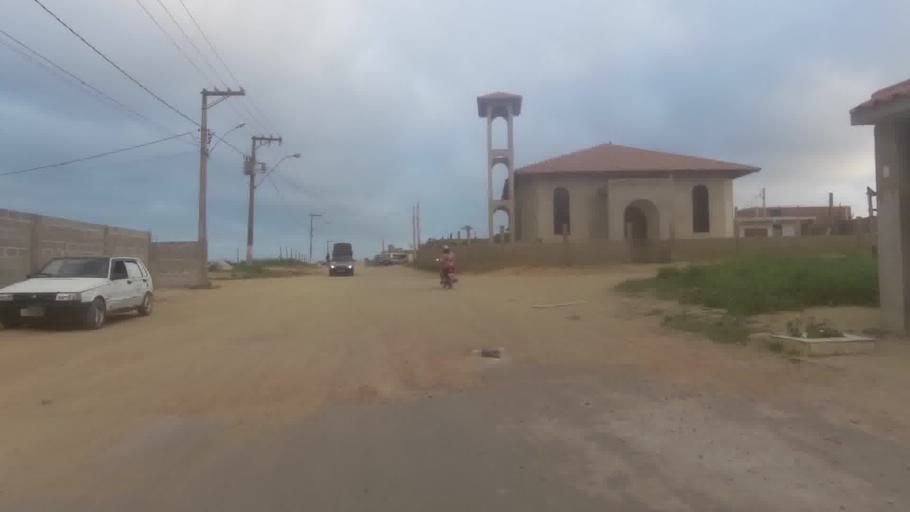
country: BR
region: Espirito Santo
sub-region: Itapemirim
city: Itapemirim
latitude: -21.0240
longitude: -40.8213
